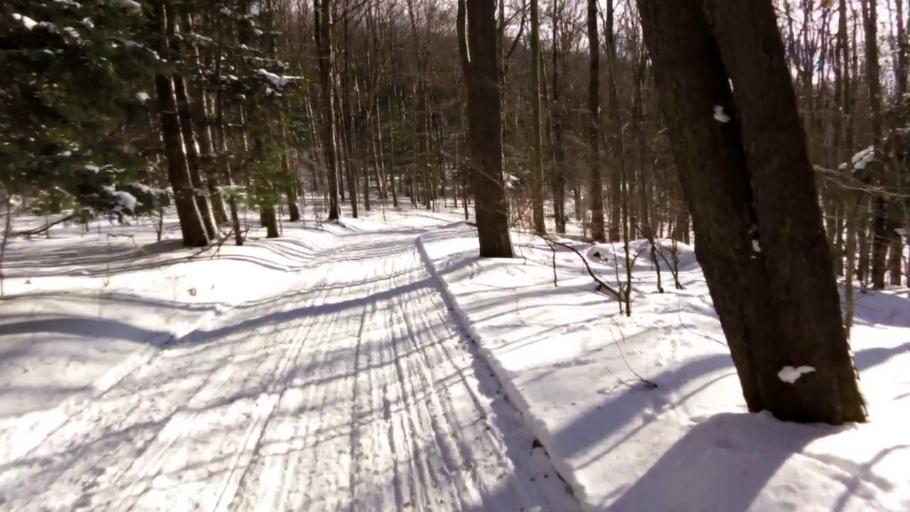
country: US
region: New York
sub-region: Cattaraugus County
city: Salamanca
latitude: 42.0675
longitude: -78.6725
